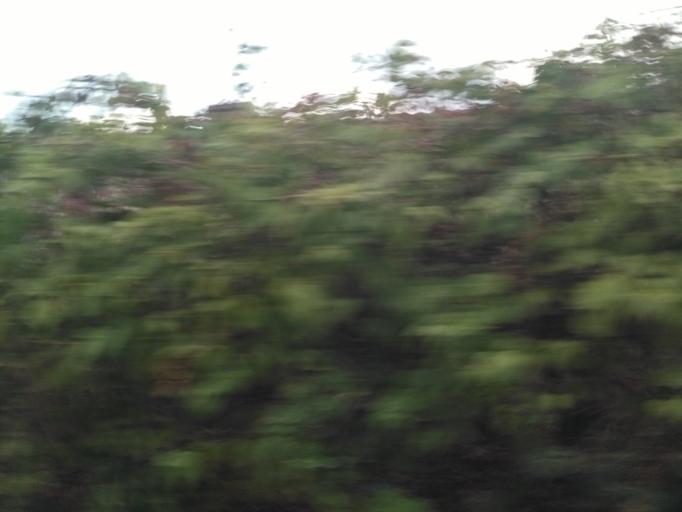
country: TZ
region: Dar es Salaam
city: Dar es Salaam
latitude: -6.8573
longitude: 39.3643
